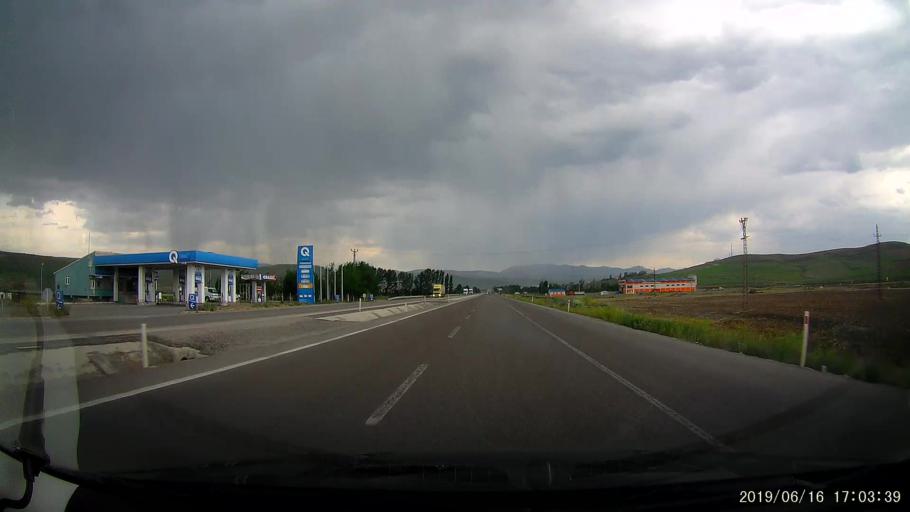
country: TR
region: Erzurum
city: Askale
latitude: 39.9344
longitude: 40.7265
